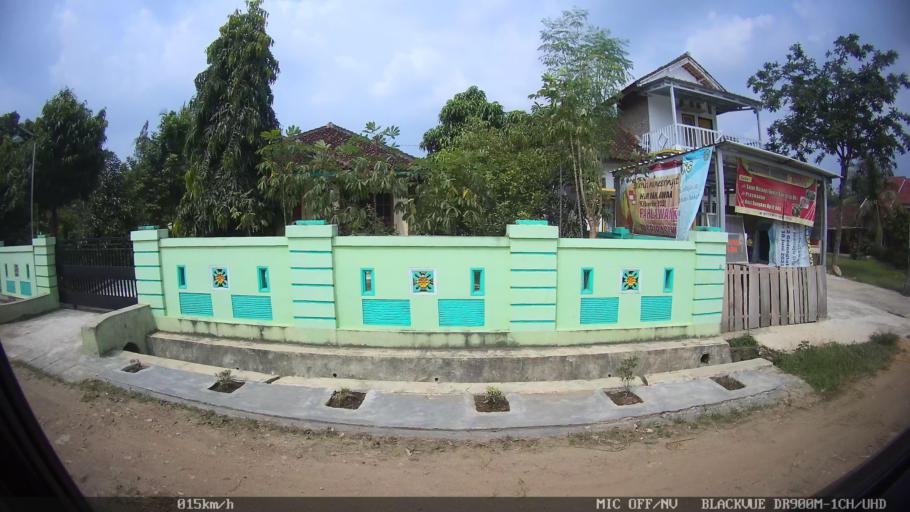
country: ID
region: Lampung
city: Gadingrejo
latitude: -5.3623
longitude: 105.0470
